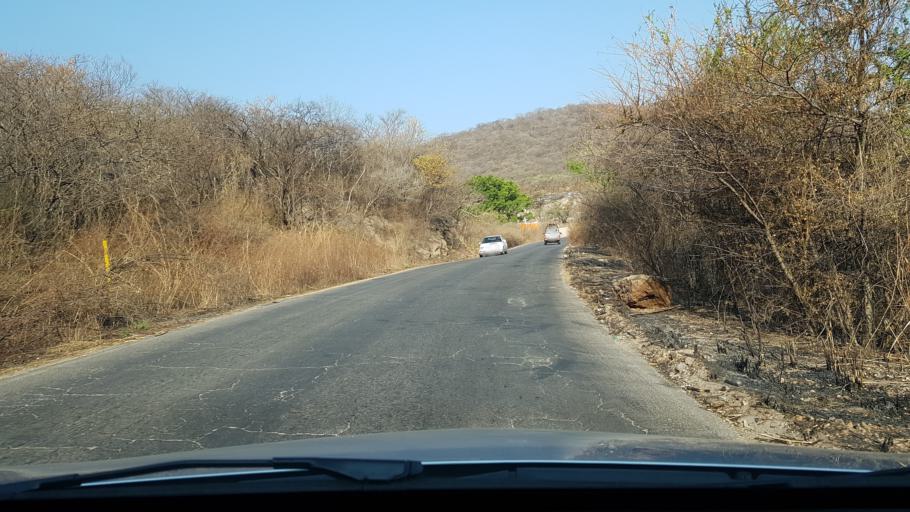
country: MX
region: Morelos
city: Tlaltizapan
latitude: 18.6579
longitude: -99.0435
